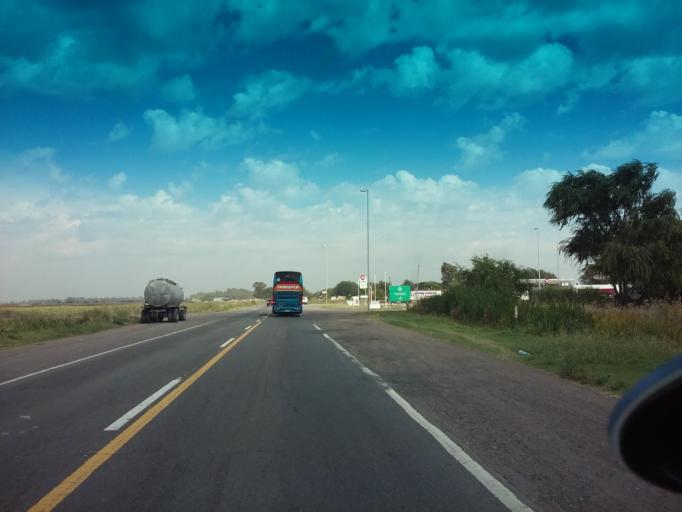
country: AR
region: Buenos Aires
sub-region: Partido de Carlos Casares
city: Carlos Casares
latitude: -35.6418
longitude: -61.3646
